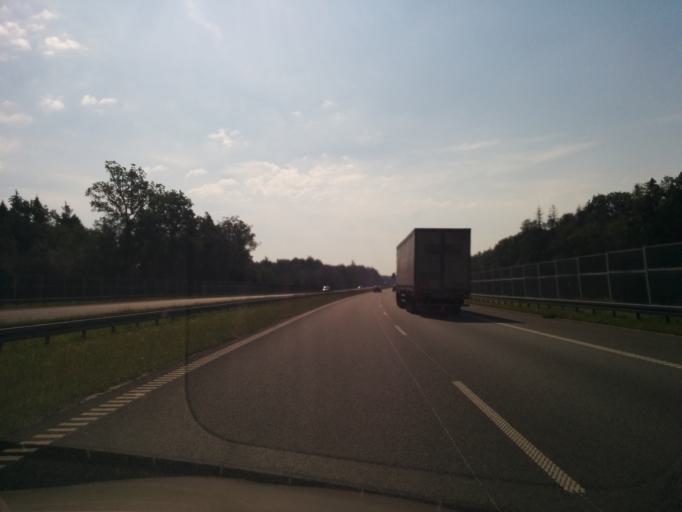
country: PL
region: Silesian Voivodeship
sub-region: Powiat tarnogorski
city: Radzionkow
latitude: 50.3866
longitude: 18.8493
